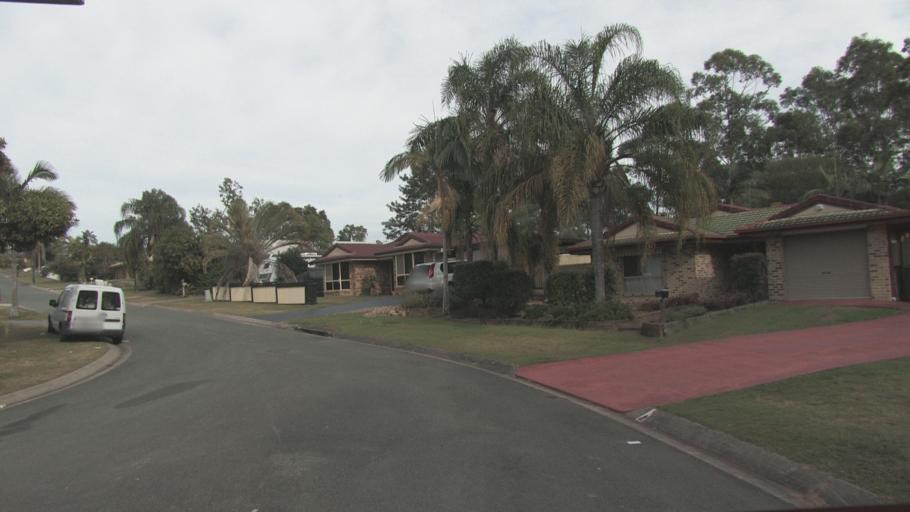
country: AU
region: Queensland
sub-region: Logan
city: Beenleigh
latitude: -27.7000
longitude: 153.1764
